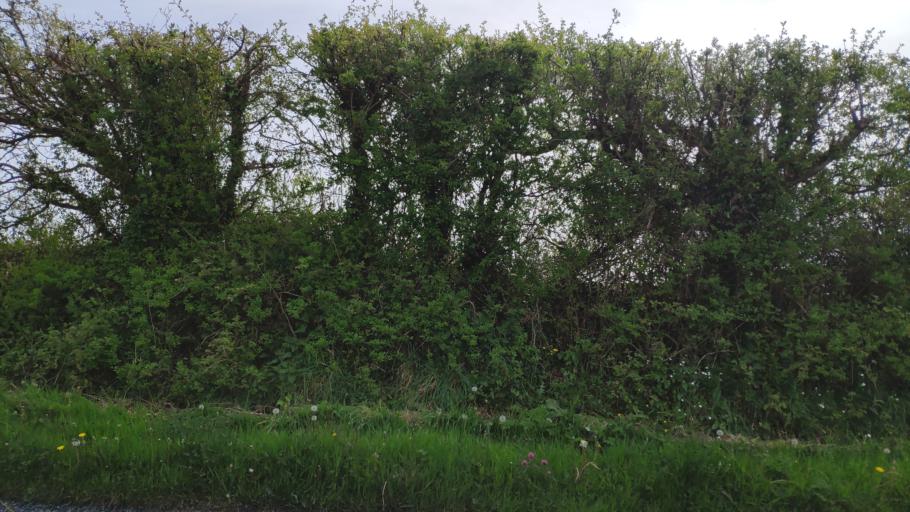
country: IE
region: Munster
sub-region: County Cork
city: Blarney
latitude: 51.9688
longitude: -8.5136
